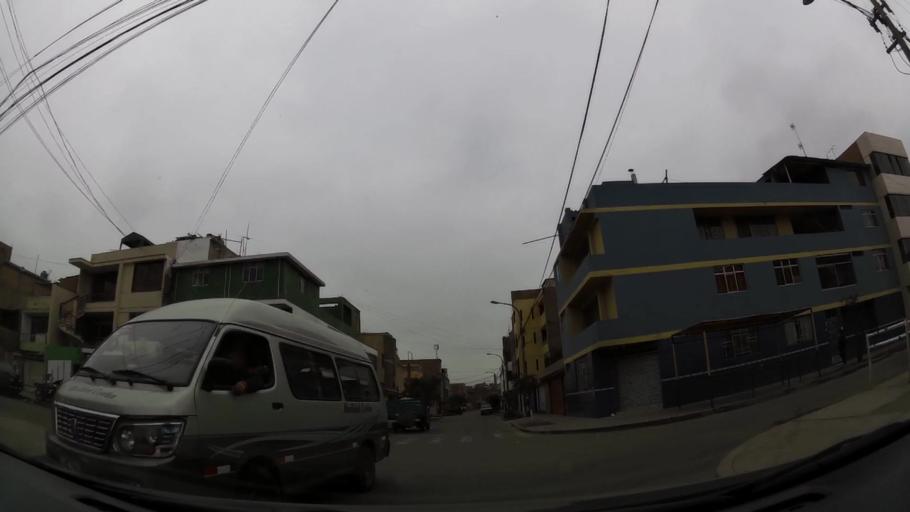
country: PE
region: Lima
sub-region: Lima
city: Independencia
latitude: -11.9710
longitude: -77.0583
